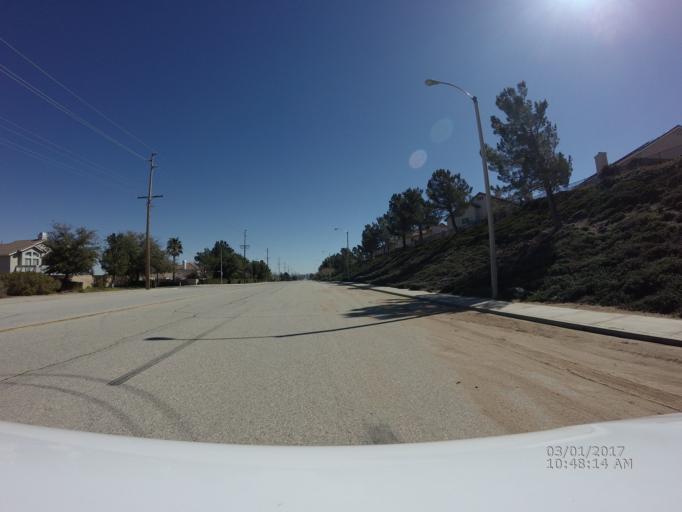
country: US
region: California
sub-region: Los Angeles County
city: Leona Valley
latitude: 34.6455
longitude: -118.2615
